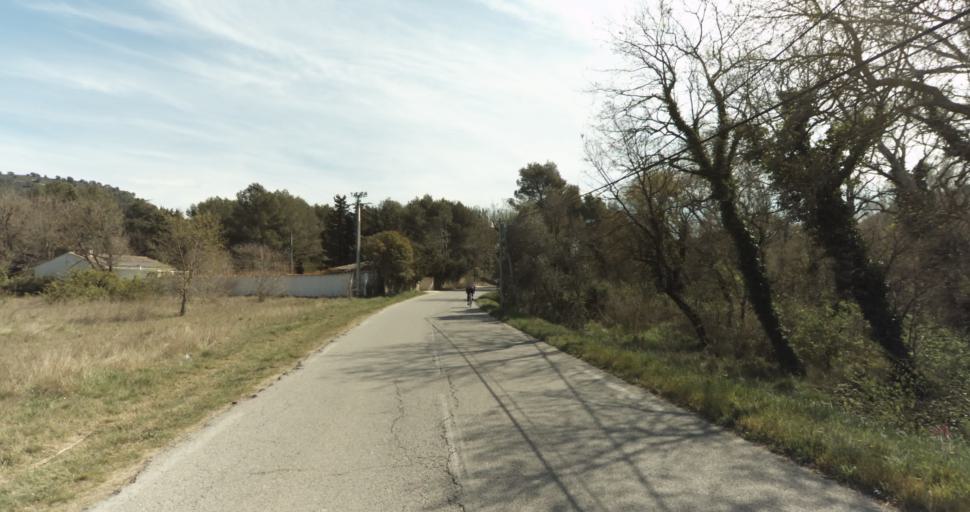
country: FR
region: Provence-Alpes-Cote d'Azur
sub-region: Departement des Bouches-du-Rhone
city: Ventabren
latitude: 43.5320
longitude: 5.2822
